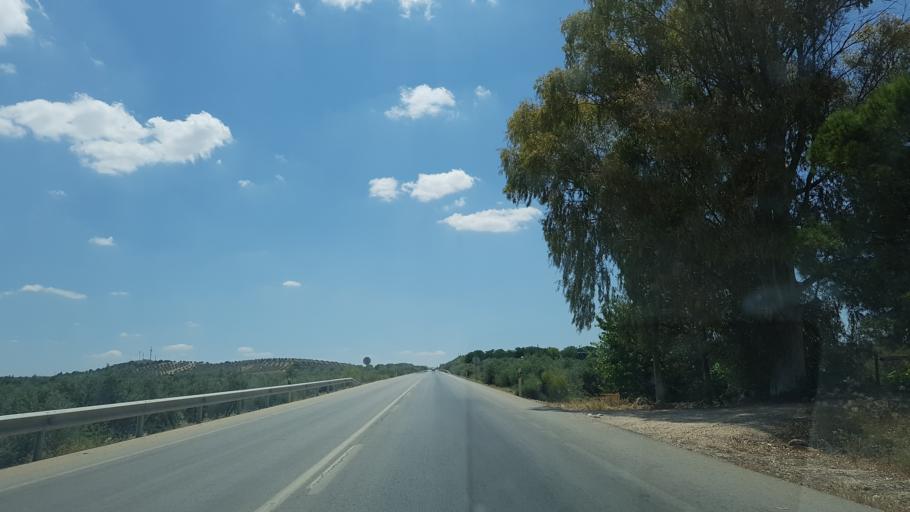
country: ES
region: Andalusia
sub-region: Province of Cordoba
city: Puente-Genil
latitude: 37.3985
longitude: -4.7809
